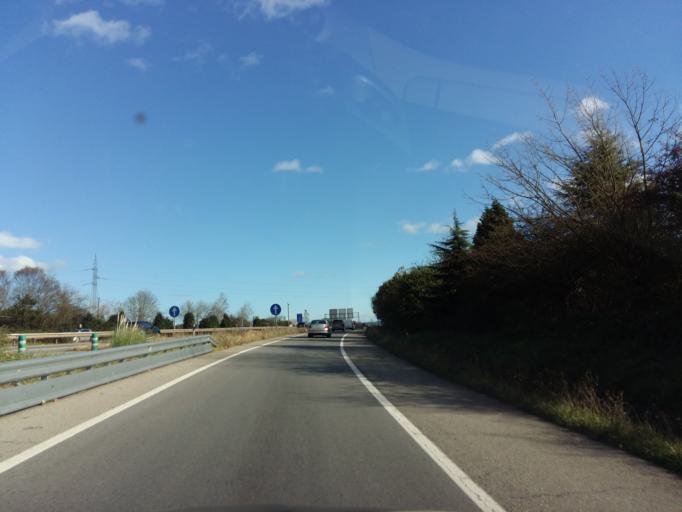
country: ES
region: Asturias
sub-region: Province of Asturias
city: Lugones
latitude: 43.3940
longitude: -5.8003
